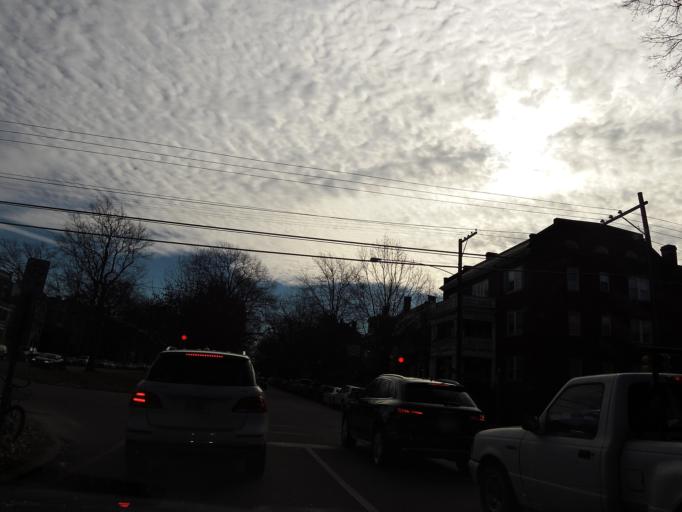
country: US
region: Virginia
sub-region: City of Richmond
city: Richmond
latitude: 37.5617
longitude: -77.4734
